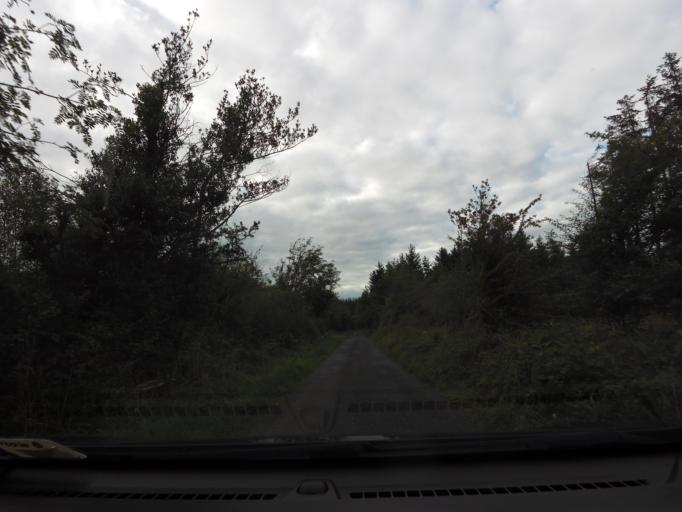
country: IE
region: Connaught
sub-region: County Galway
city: Loughrea
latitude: 53.1364
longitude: -8.5220
